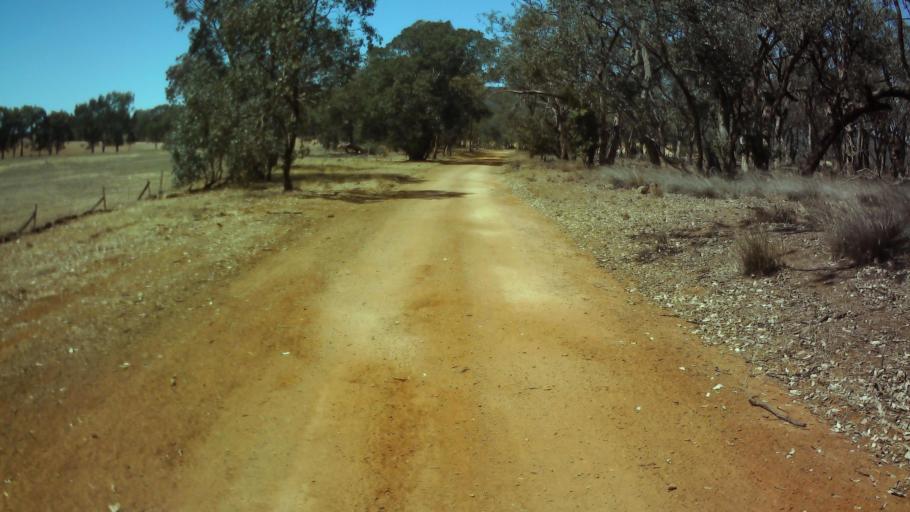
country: AU
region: New South Wales
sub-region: Weddin
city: Grenfell
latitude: -33.9529
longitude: 148.0847
